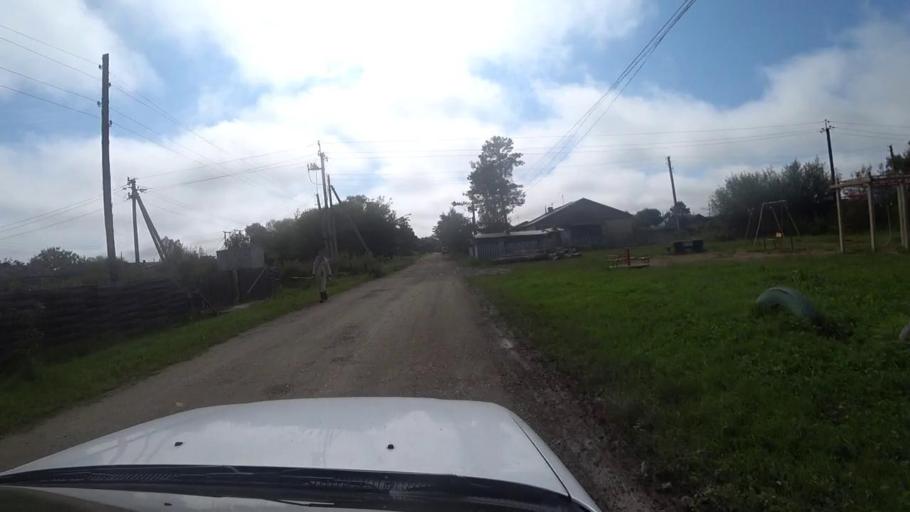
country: RU
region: Primorskiy
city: Dal'nerechensk
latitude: 45.9184
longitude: 133.7237
